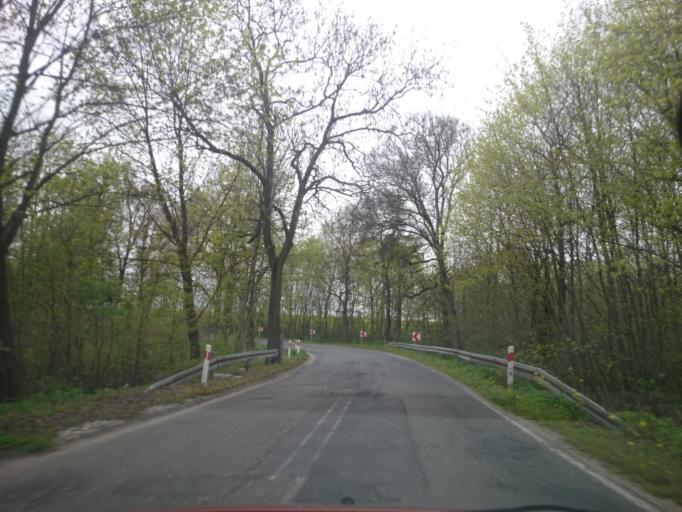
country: PL
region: Lower Silesian Voivodeship
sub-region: Powiat strzelinski
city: Przeworno
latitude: 50.6407
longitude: 17.1482
